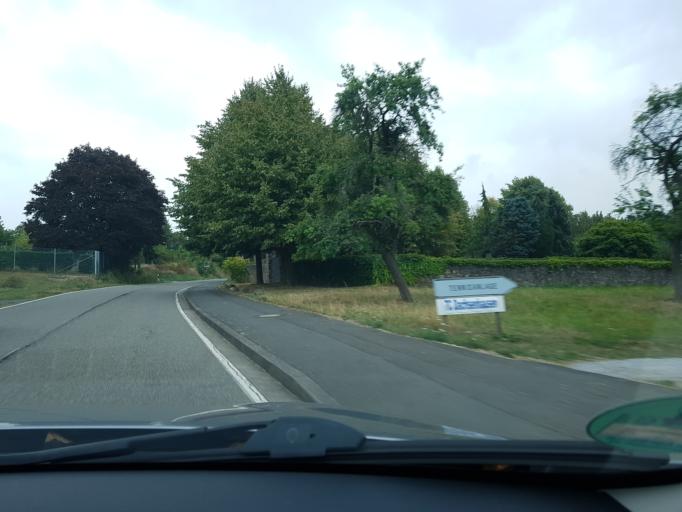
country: DE
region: Rheinland-Pfalz
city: Dachsenhausen
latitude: 50.2520
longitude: 7.7289
